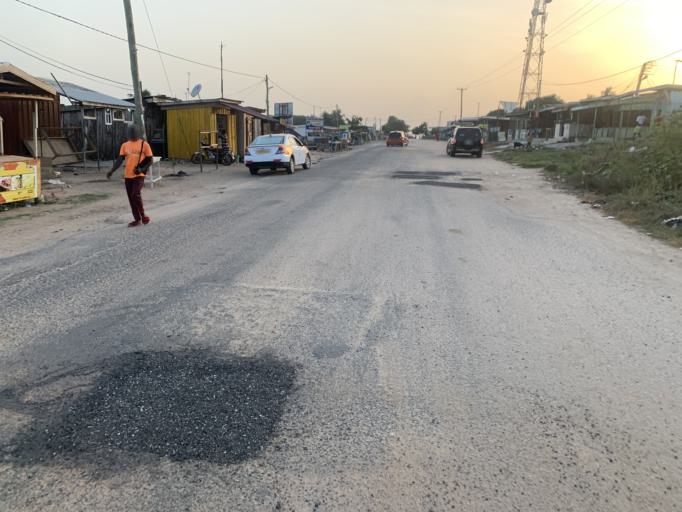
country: GH
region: Central
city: Winneba
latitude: 5.3543
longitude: -0.6149
